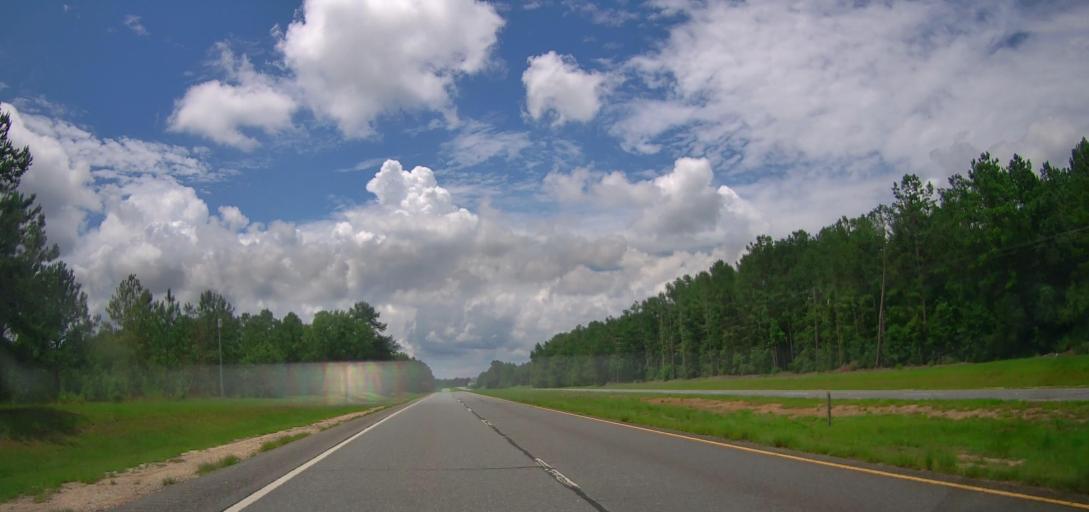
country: US
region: Georgia
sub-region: Dodge County
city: Eastman
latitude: 32.1882
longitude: -83.2028
